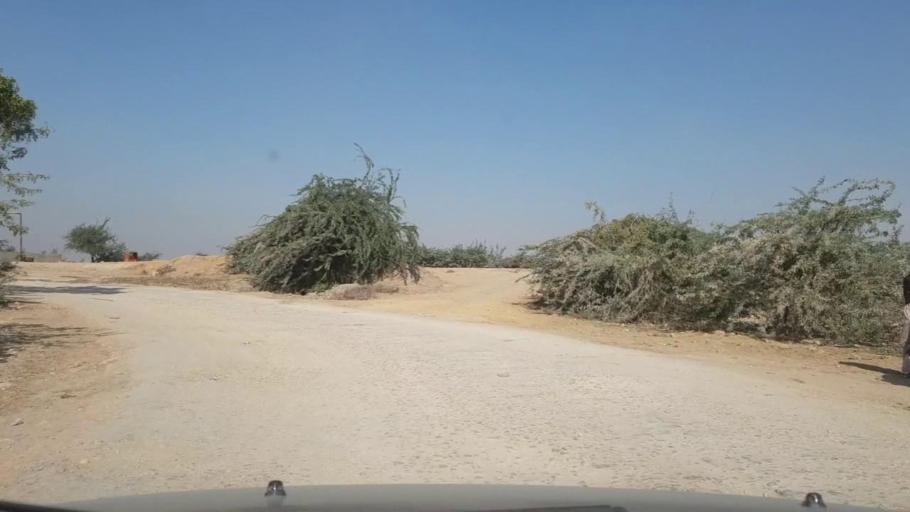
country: PK
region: Sindh
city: Thatta
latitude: 24.8022
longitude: 67.9020
